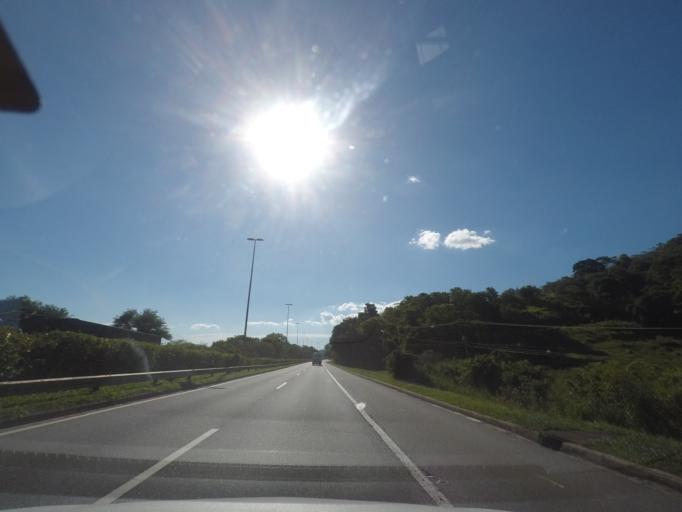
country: BR
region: Rio de Janeiro
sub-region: Sao Goncalo
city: Sao Goncalo
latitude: -22.6655
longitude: -43.0999
